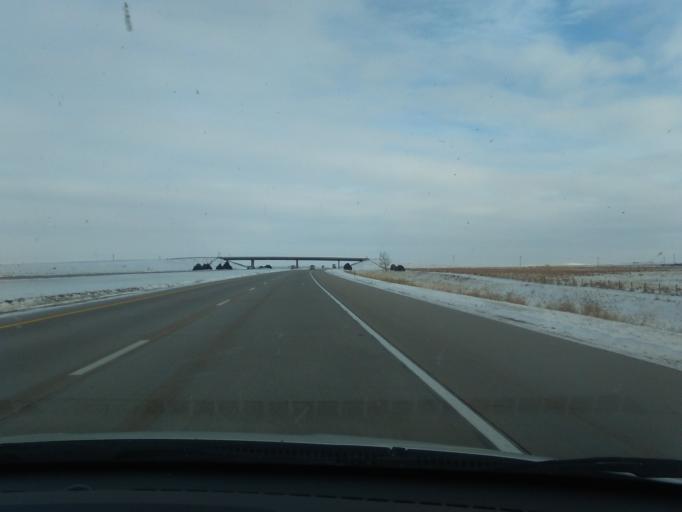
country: US
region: Nebraska
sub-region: Deuel County
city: Chappell
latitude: 41.1093
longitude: -102.5577
